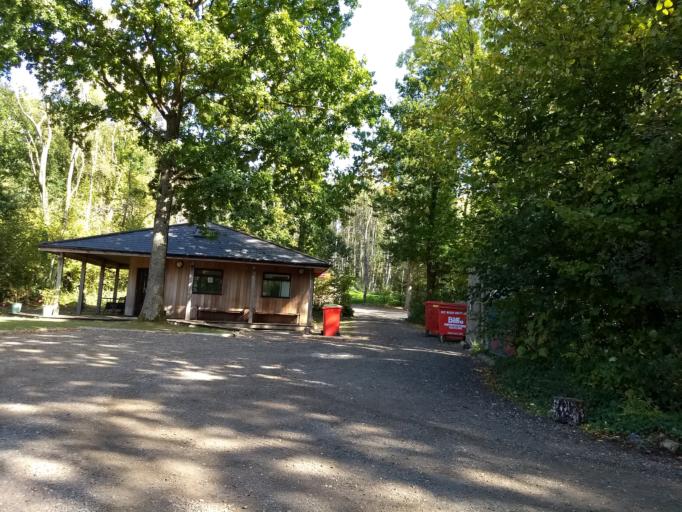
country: GB
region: England
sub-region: Isle of Wight
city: Brading
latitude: 50.7013
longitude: -1.1437
